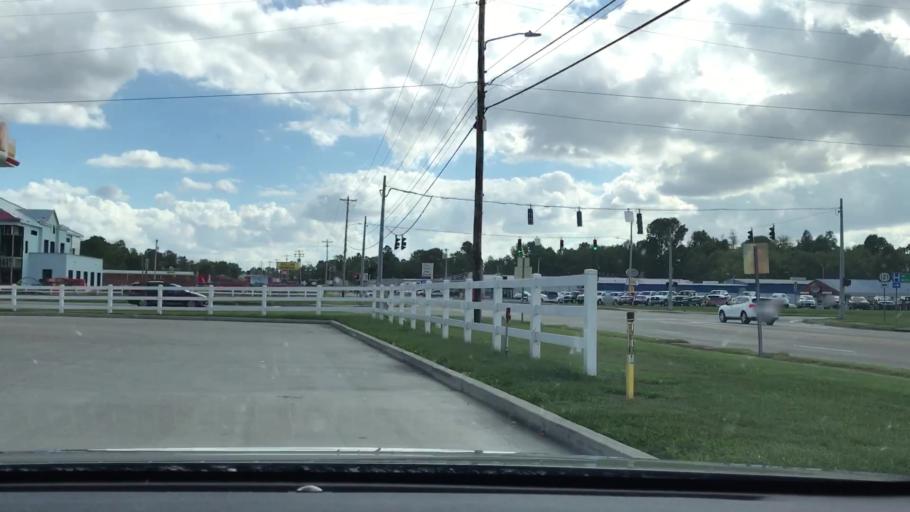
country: US
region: Kentucky
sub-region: Graves County
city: Mayfield
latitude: 36.7558
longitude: -88.6400
